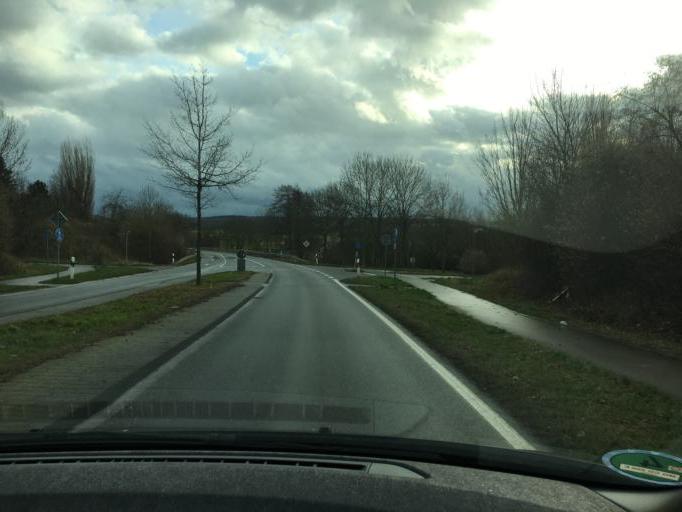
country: DE
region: North Rhine-Westphalia
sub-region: Regierungsbezirk Koln
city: Euskirchen
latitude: 50.6526
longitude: 6.7456
